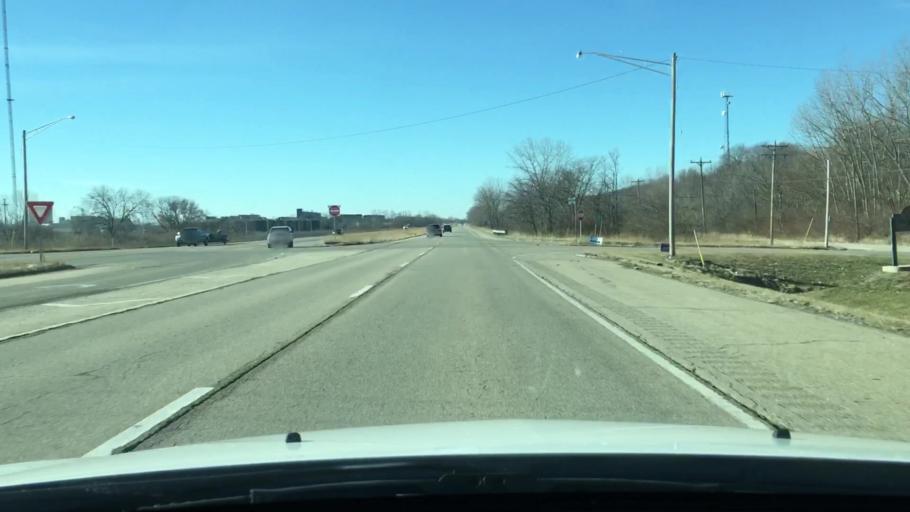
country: US
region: Illinois
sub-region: Peoria County
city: Glasford
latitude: 40.5656
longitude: -89.7308
